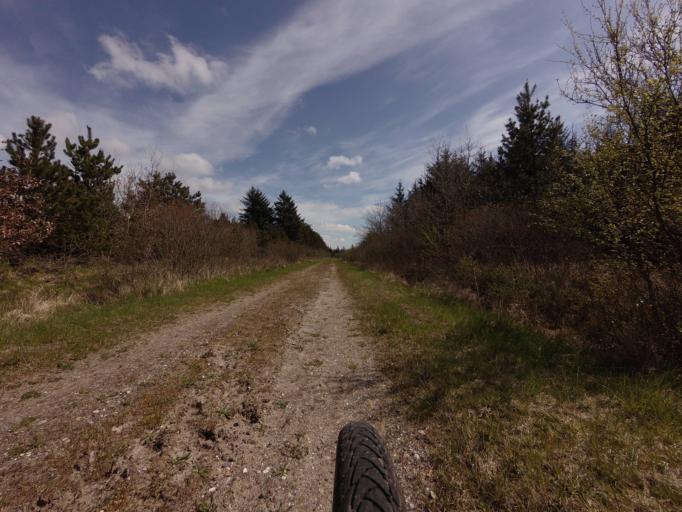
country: DK
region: North Denmark
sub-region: Jammerbugt Kommune
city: Brovst
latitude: 57.1696
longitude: 9.5659
